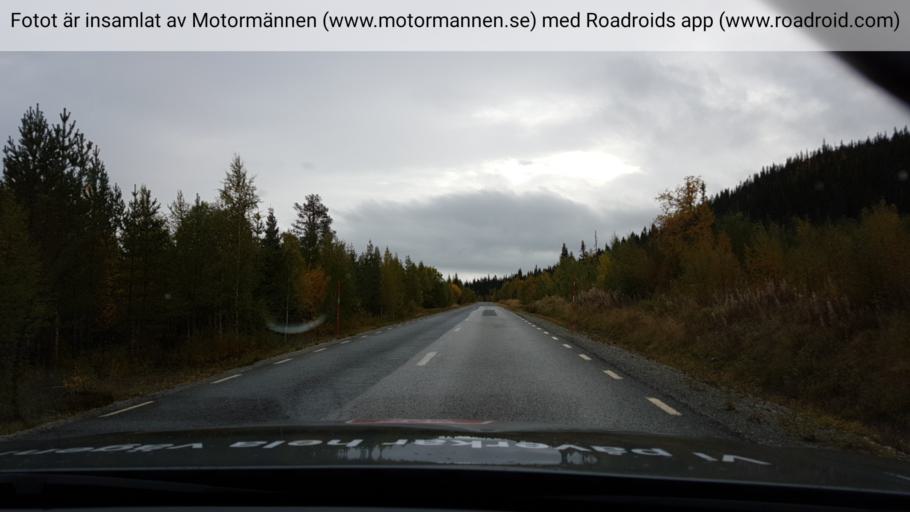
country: SE
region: Vaesterbotten
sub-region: Vilhelmina Kommun
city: Sjoberg
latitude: 64.8873
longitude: 15.8636
